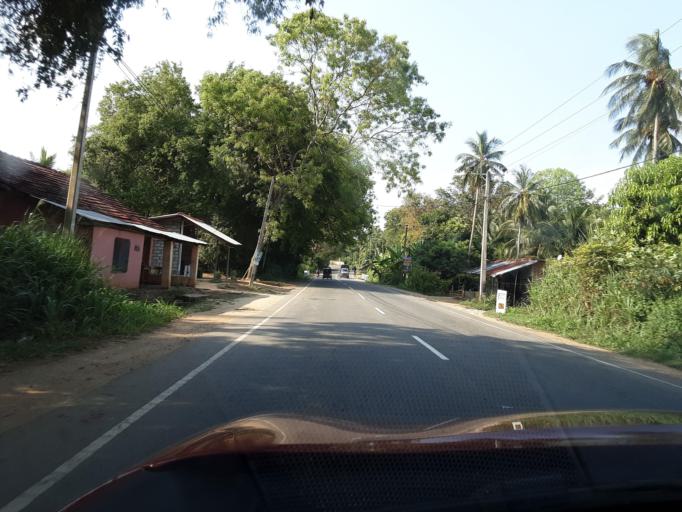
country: LK
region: Uva
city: Haputale
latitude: 6.5930
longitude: 81.1420
